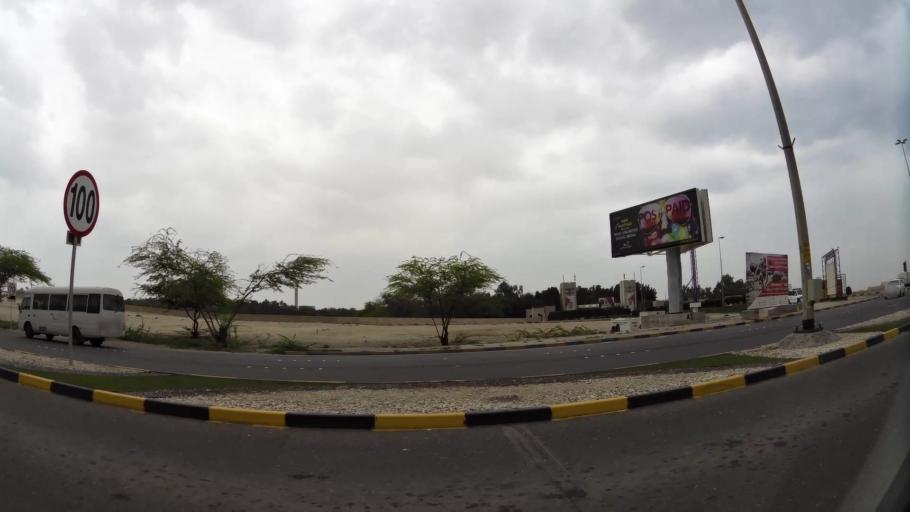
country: BH
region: Central Governorate
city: Dar Kulayb
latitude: 26.0582
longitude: 50.5094
